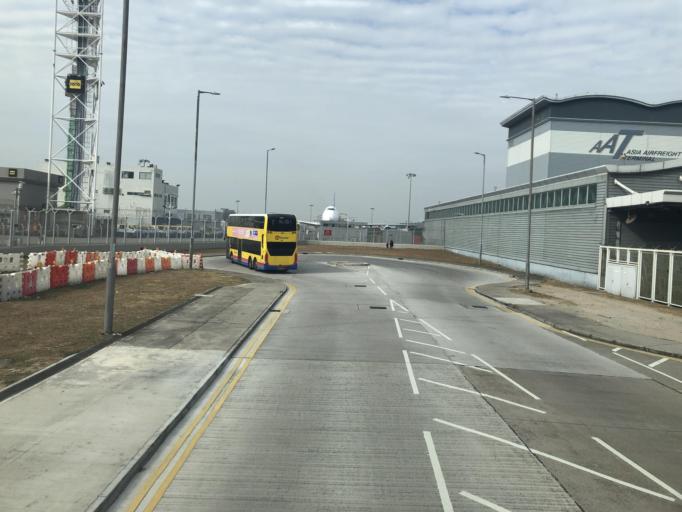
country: HK
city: Tai O
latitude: 22.2964
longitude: 113.9206
